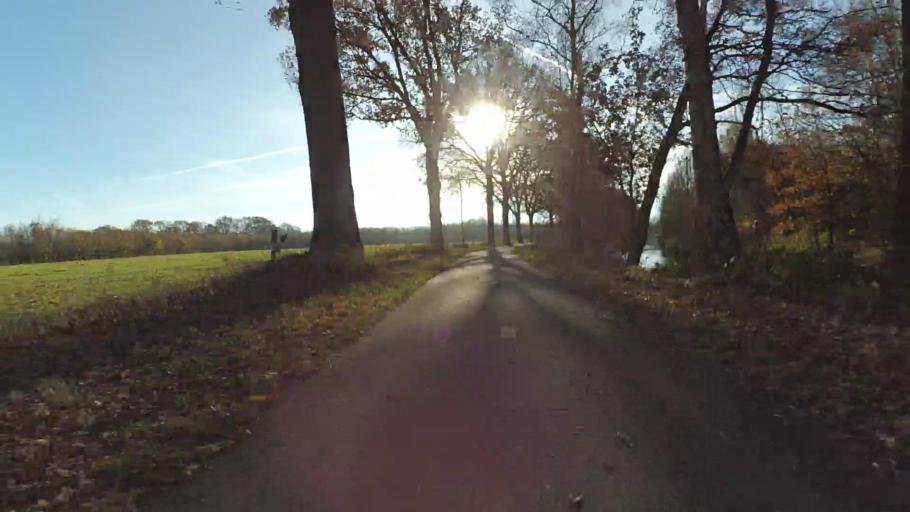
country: NL
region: Utrecht
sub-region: Gemeente Utrechtse Heuvelrug
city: Overberg
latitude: 52.0710
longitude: 5.4778
